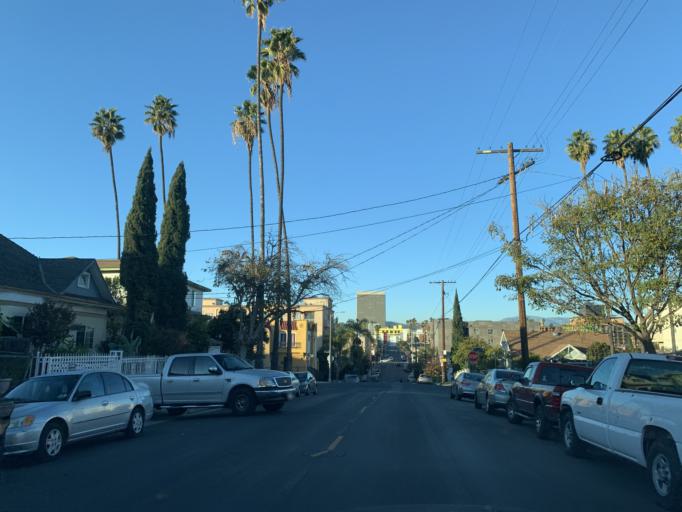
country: US
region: California
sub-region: Los Angeles County
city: Silver Lake
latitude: 34.0504
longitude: -118.2979
